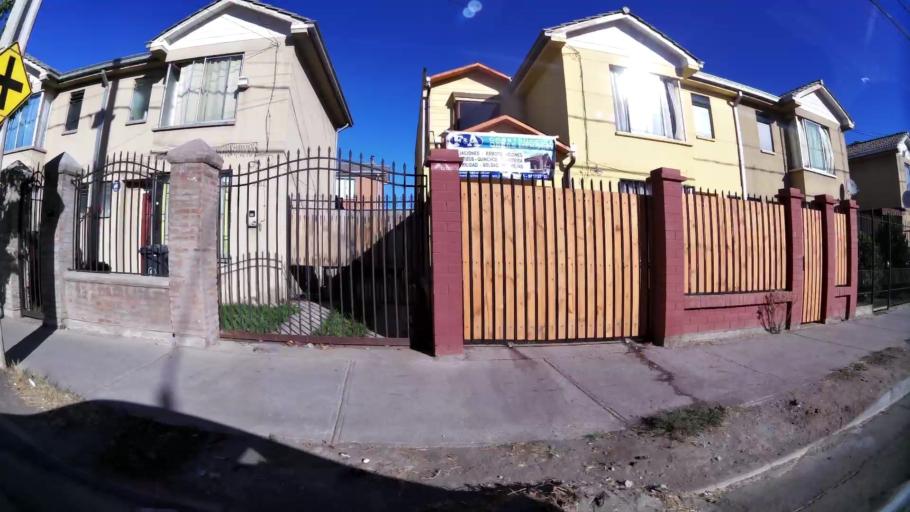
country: CL
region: O'Higgins
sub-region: Provincia de Cachapoal
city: Rancagua
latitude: -34.1834
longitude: -70.7619
